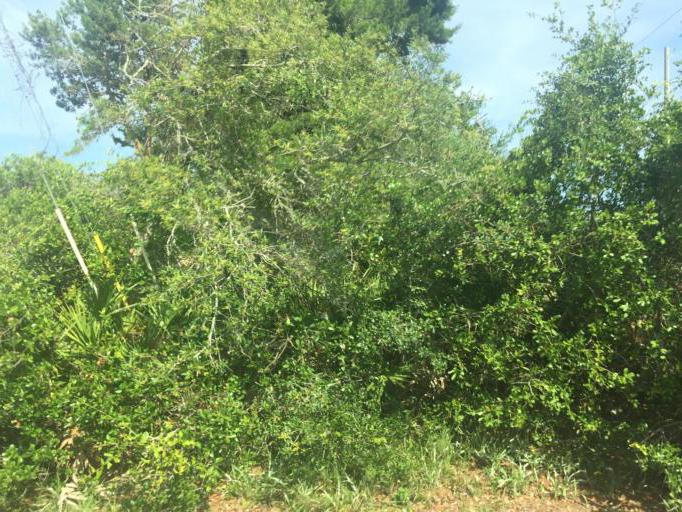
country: US
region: Florida
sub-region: Bay County
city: Laguna Beach
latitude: 30.2502
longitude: -85.9305
